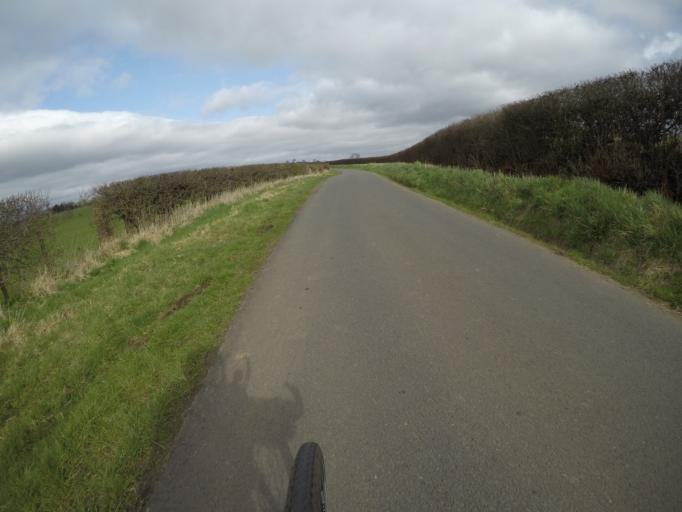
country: GB
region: Scotland
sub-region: North Ayrshire
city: Irvine
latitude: 55.6396
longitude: -4.6298
